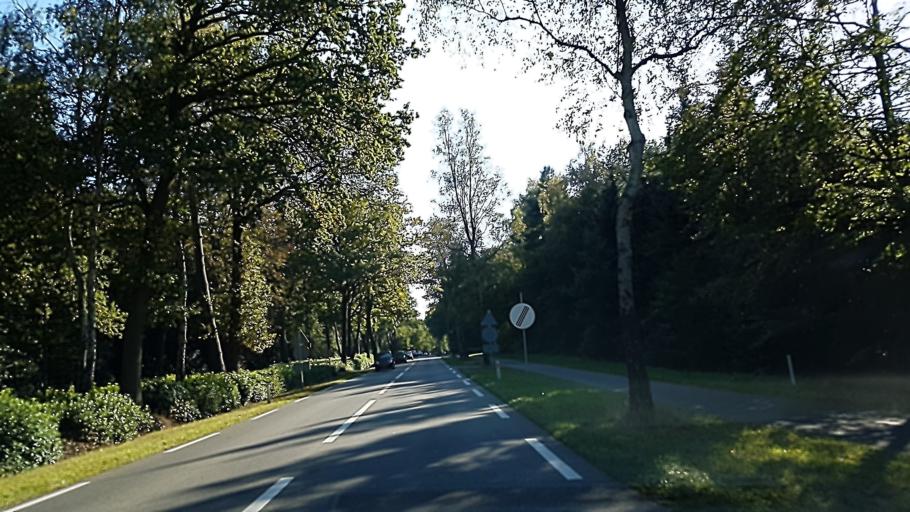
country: NL
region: North Brabant
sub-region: Gemeente Woensdrecht
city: Woensdrecht
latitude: 51.4027
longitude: 4.3549
